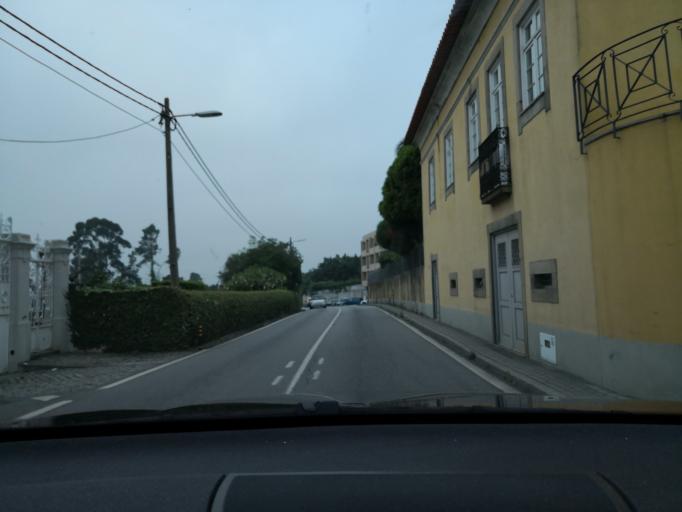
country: PT
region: Aveiro
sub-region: Santa Maria da Feira
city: Lamas
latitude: 41.0009
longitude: -8.5655
